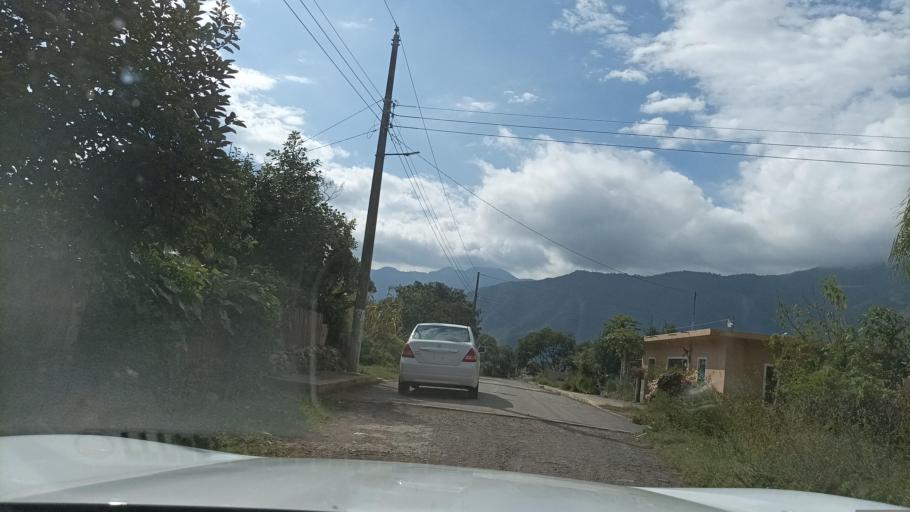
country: MX
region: Veracruz
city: Maltrata
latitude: 18.8165
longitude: -97.2557
